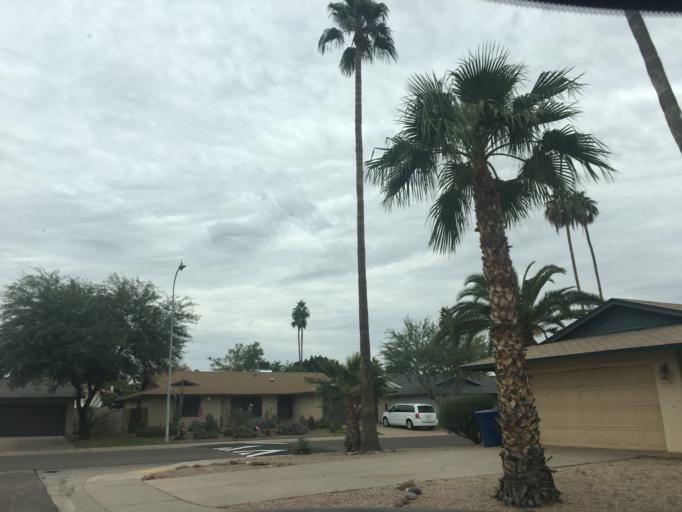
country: US
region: Arizona
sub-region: Maricopa County
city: Tempe
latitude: 33.3826
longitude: -111.9135
